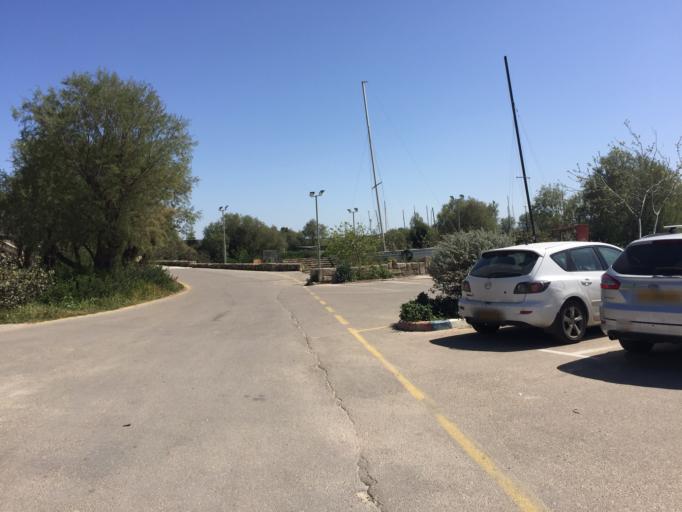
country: IL
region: Haifa
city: Qesarya
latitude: 32.4901
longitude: 34.8902
